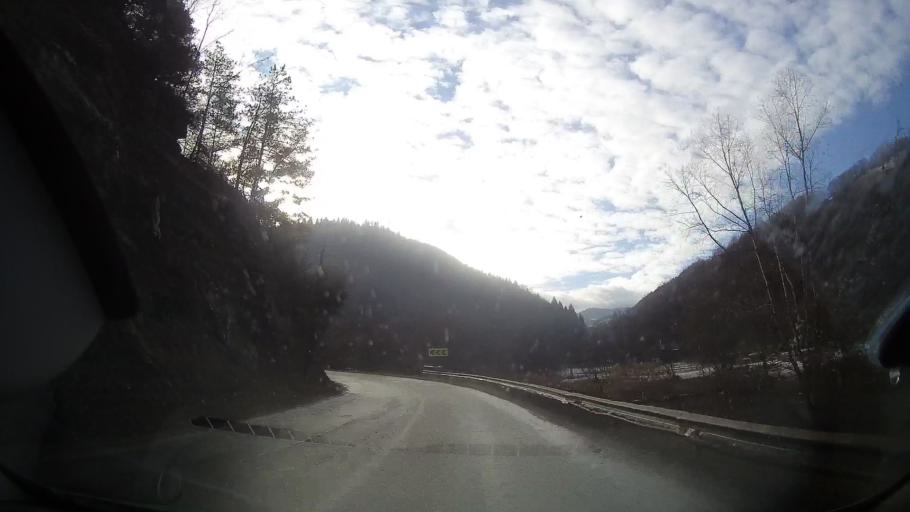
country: RO
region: Alba
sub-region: Comuna Bistra
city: Bistra
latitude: 46.3802
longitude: 23.1456
